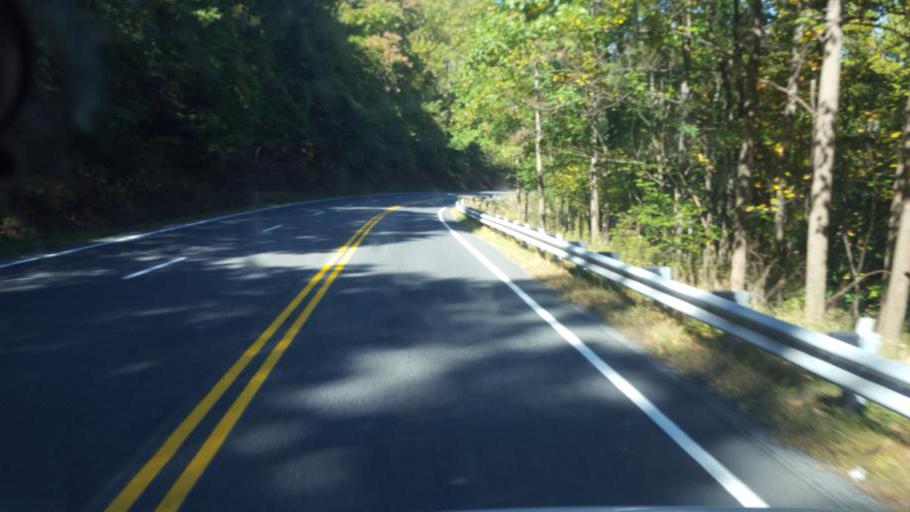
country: US
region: Virginia
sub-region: Rockingham County
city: Elkton
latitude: 38.3676
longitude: -78.5640
